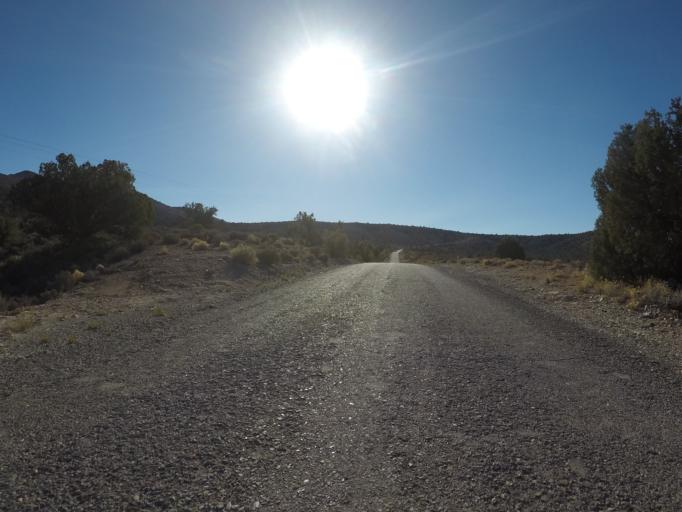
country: US
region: Nevada
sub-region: Clark County
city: Summerlin South
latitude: 36.0920
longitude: -115.5632
